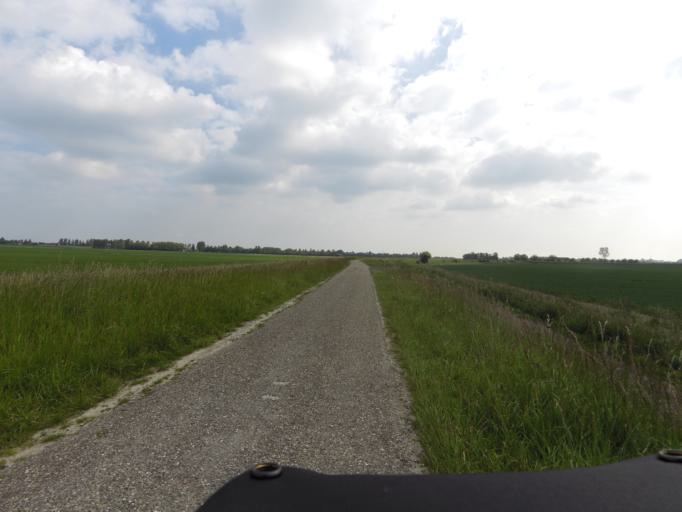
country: NL
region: Zeeland
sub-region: Gemeente Noord-Beveland
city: Kamperland
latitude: 51.5817
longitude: 3.7125
